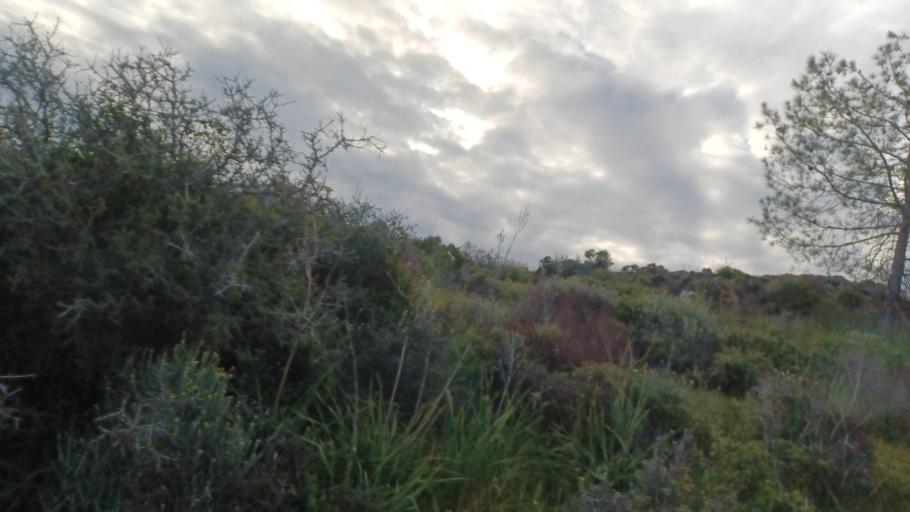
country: CY
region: Lefkosia
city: Lefka
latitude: 35.0788
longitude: 32.8980
